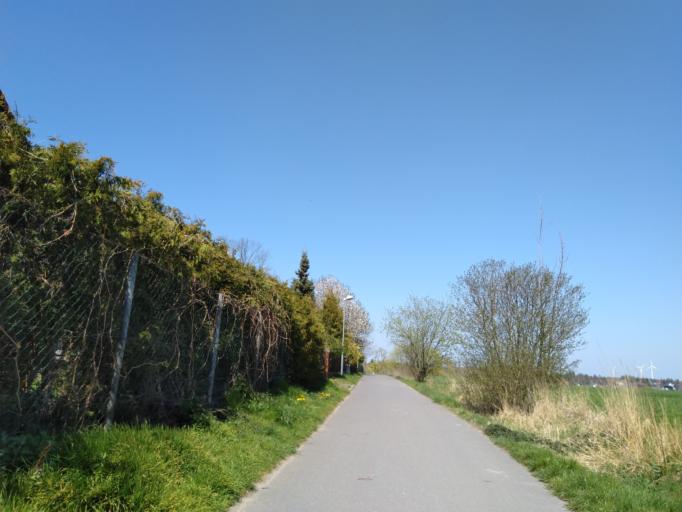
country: DE
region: Brandenburg
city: Bernau bei Berlin
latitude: 52.6896
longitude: 13.5887
